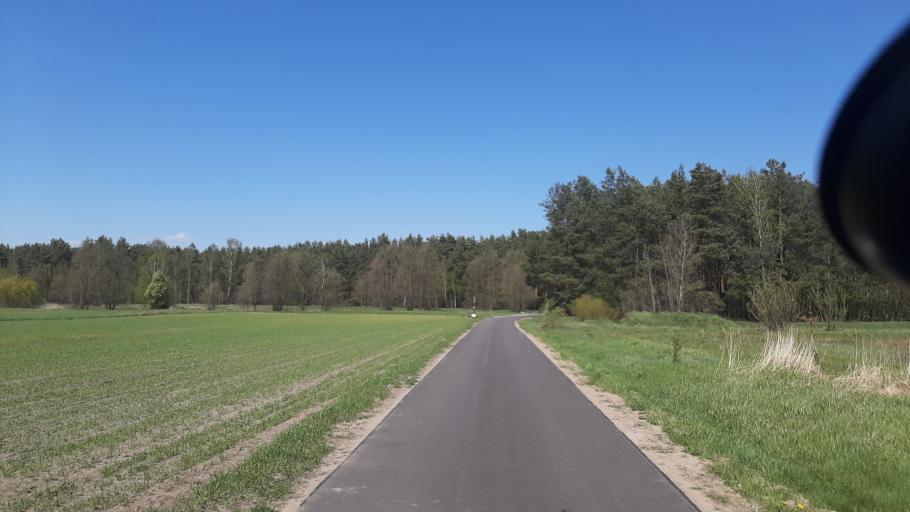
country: PL
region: Lublin Voivodeship
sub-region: Powiat lubartowski
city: Abramow
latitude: 51.4066
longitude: 22.3228
